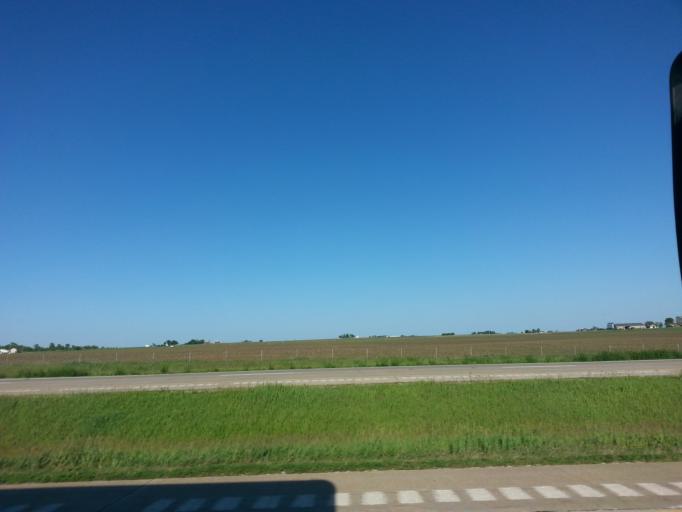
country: US
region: Illinois
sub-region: Woodford County
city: El Paso
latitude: 40.7762
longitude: -89.0351
